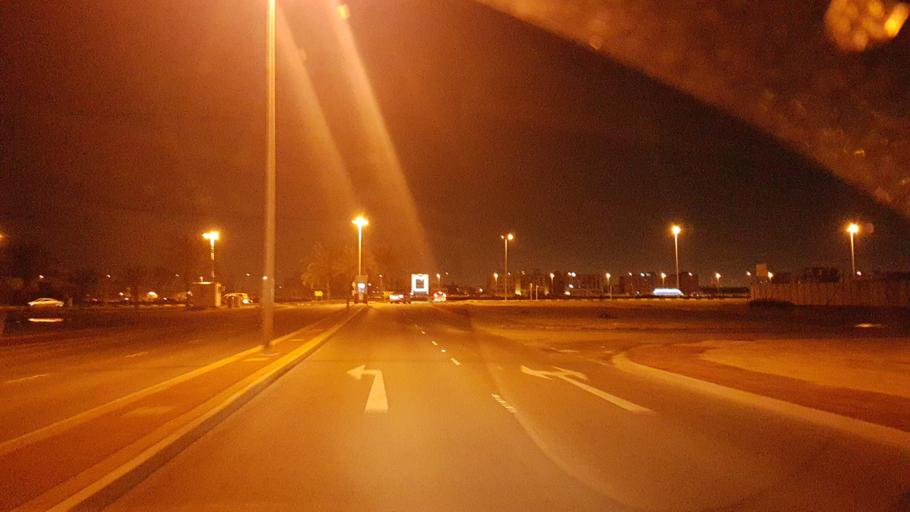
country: BH
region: Muharraq
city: Al Hadd
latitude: 26.2826
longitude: 50.6580
